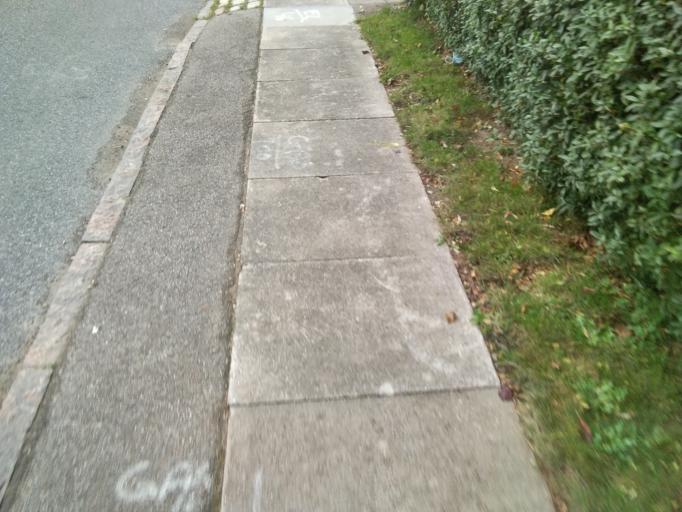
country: DK
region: Capital Region
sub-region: Rodovre Kommune
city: Rodovre
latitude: 55.7062
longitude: 12.4630
